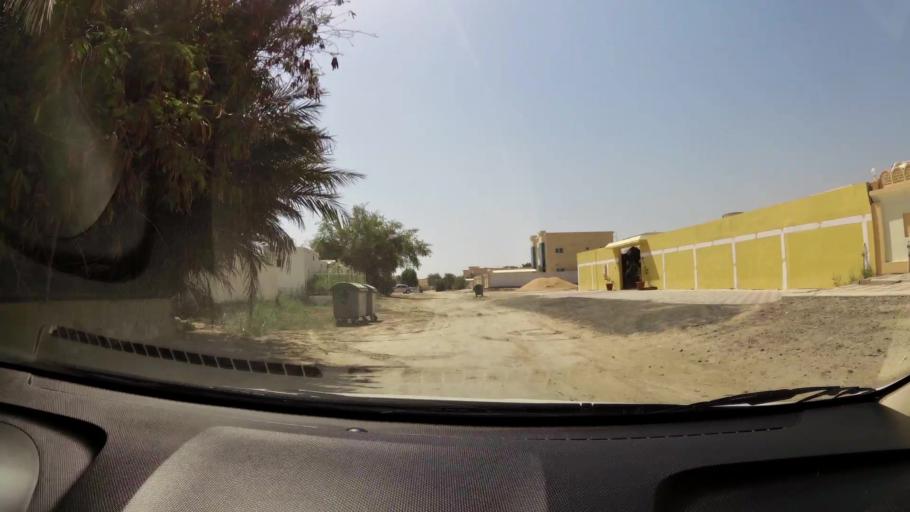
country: AE
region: Ajman
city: Ajman
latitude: 25.4137
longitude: 55.4788
